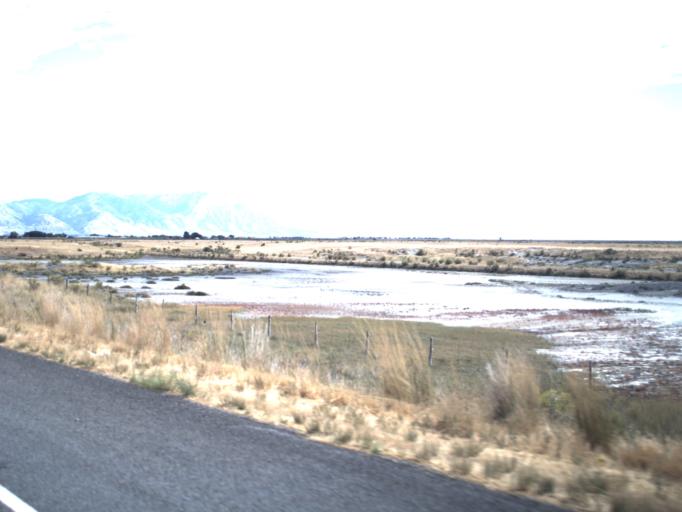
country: US
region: Utah
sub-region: Box Elder County
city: Elwood
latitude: 41.5781
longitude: -112.2413
